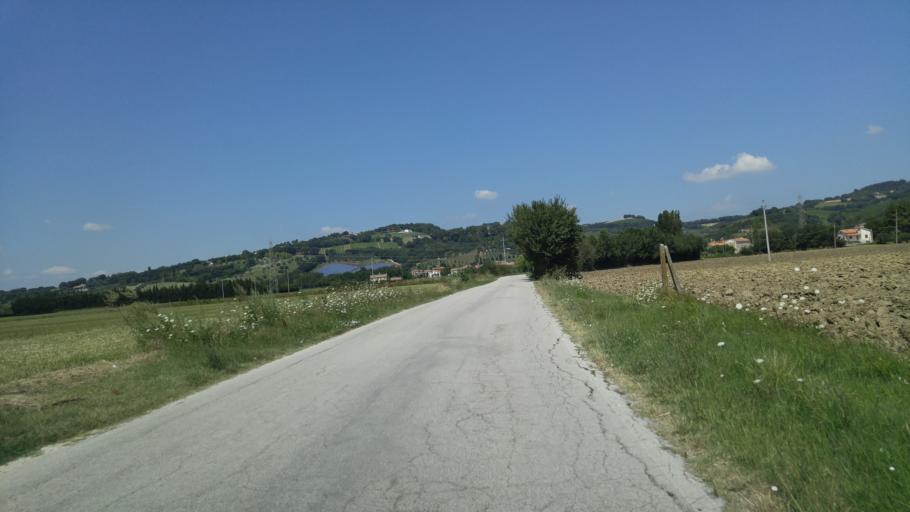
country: IT
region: The Marches
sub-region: Provincia di Pesaro e Urbino
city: Cuccurano
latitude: 43.7934
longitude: 12.9774
